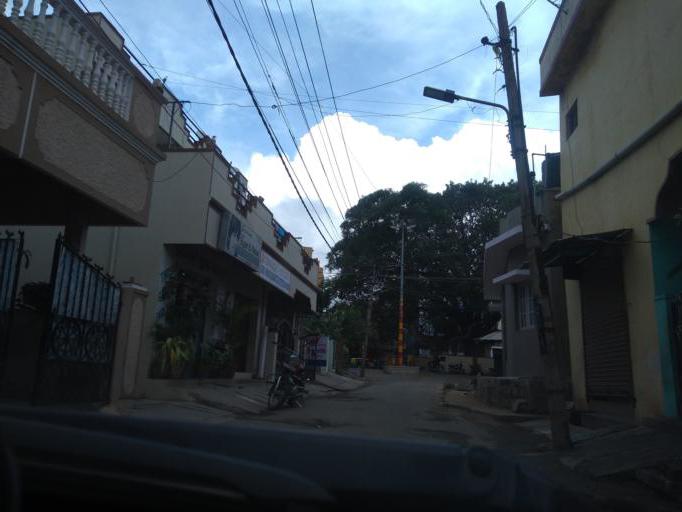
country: IN
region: Karnataka
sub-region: Bangalore Urban
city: Bangalore
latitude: 13.0103
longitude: 77.6593
